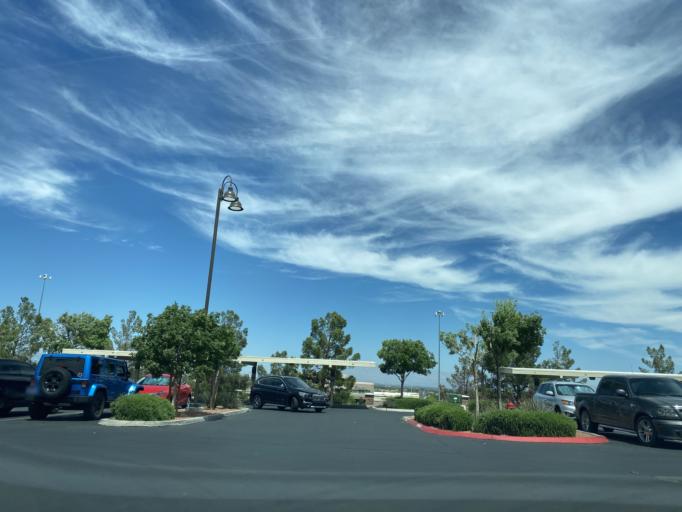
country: US
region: Nevada
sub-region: Clark County
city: Whitney
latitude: 36.0236
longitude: -115.0831
